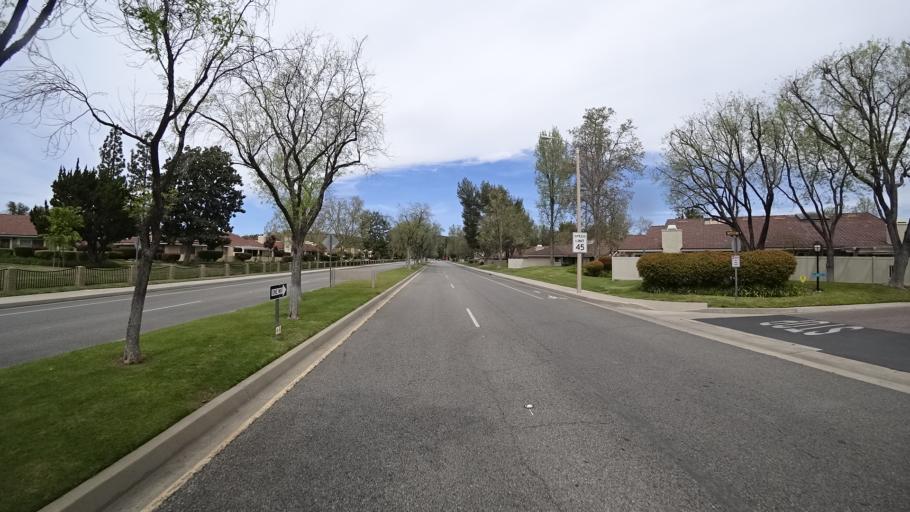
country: US
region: California
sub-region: Ventura County
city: Thousand Oaks
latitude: 34.1452
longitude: -118.8355
